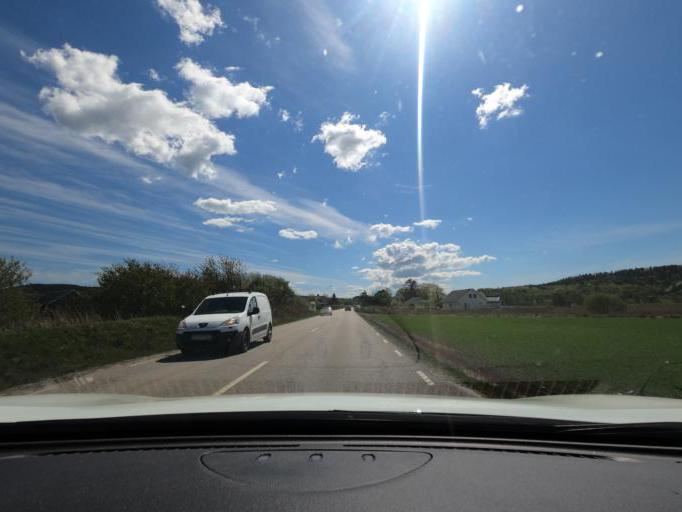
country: SE
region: Halland
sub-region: Kungsbacka Kommun
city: Fjaeras kyrkby
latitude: 57.4256
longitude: 12.1951
